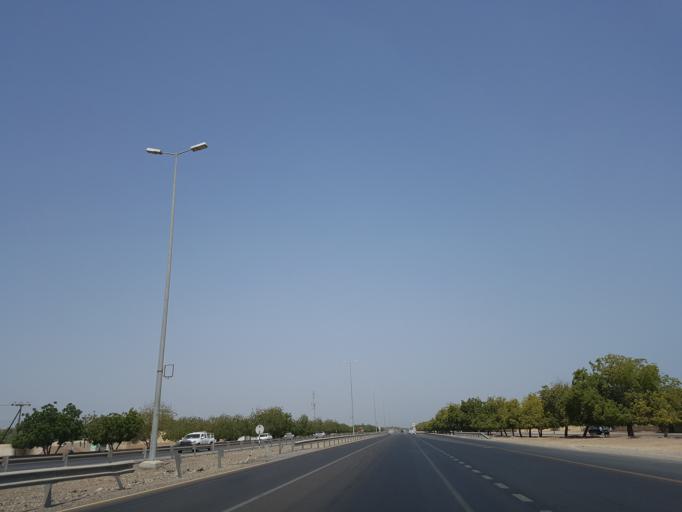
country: OM
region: Al Batinah
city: Saham
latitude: 24.0814
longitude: 56.9386
